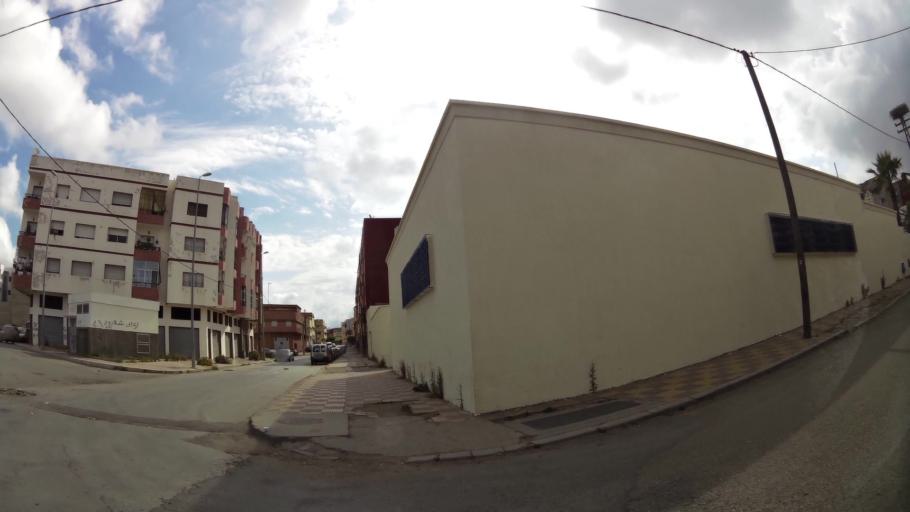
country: MA
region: Gharb-Chrarda-Beni Hssen
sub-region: Kenitra Province
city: Kenitra
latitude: 34.2661
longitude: -6.5670
